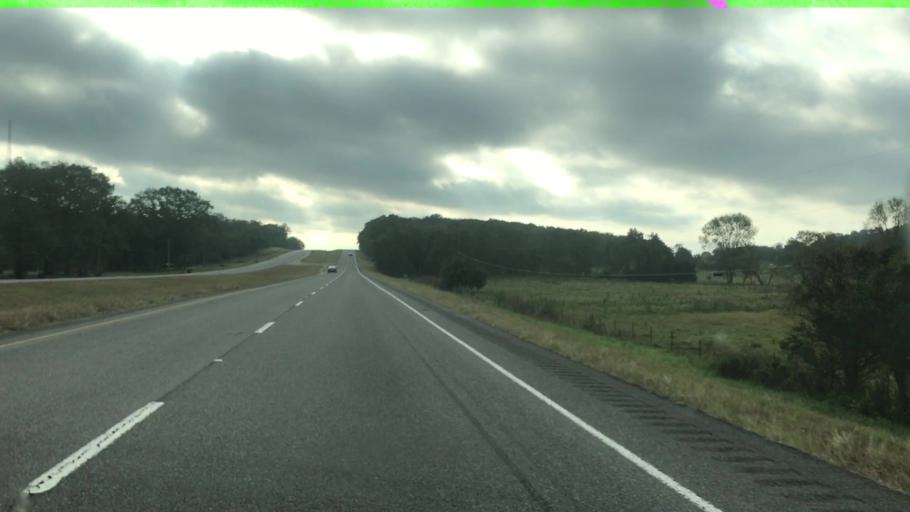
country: US
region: Alabama
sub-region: Morgan County
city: Danville
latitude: 34.4011
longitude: -87.1332
